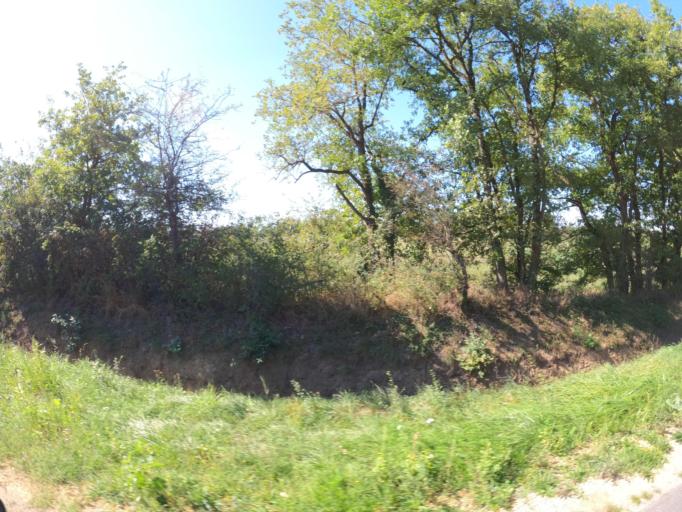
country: FR
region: Poitou-Charentes
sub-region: Departement de la Vienne
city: Saulge
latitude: 46.3933
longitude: 0.9046
